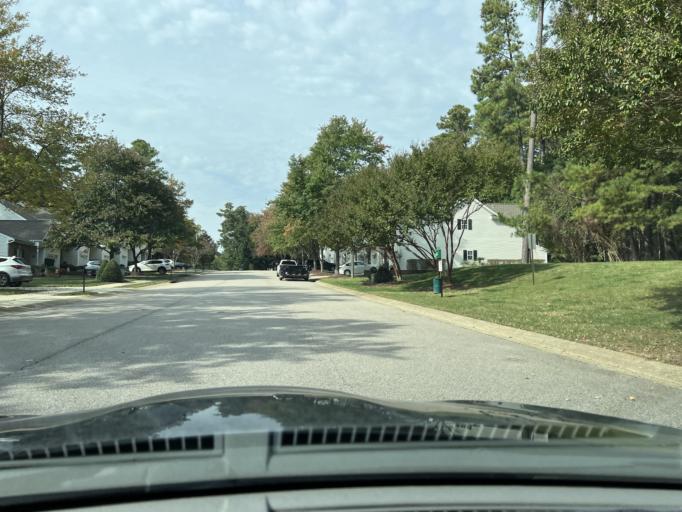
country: US
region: North Carolina
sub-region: Wake County
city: Wake Forest
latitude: 35.8904
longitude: -78.5917
